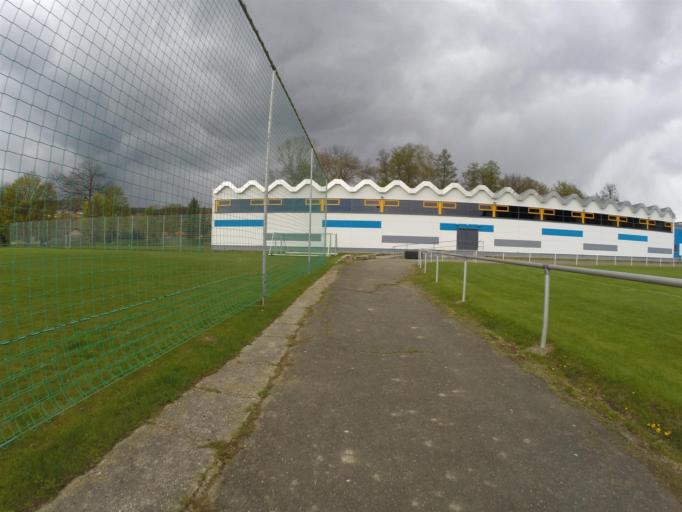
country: DE
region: Thuringia
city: Jena
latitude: 50.9129
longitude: 11.5816
